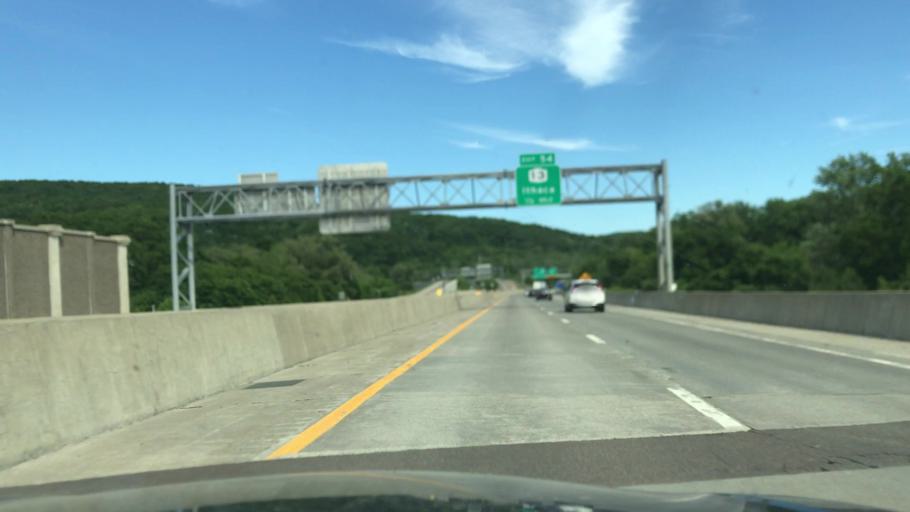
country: US
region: New York
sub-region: Chemung County
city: Horseheads
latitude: 42.1554
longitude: -76.8146
